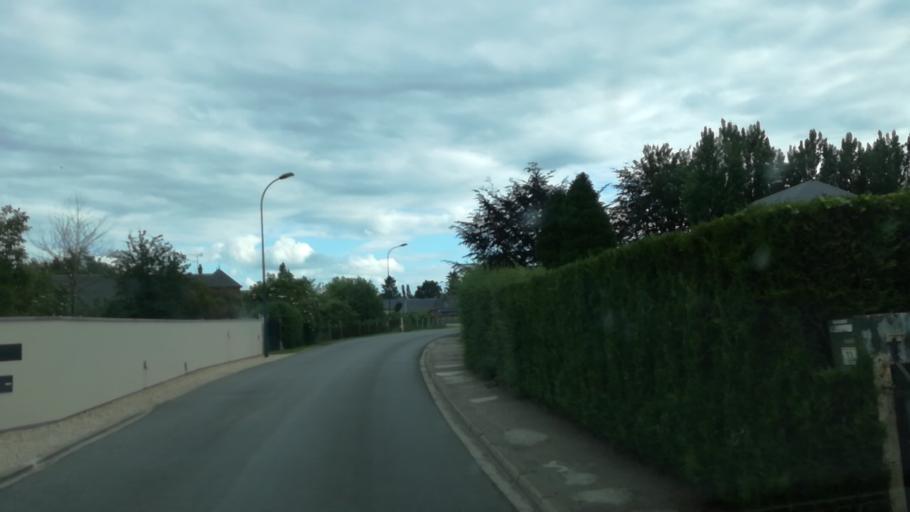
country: FR
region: Haute-Normandie
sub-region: Departement de l'Eure
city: Bourgtheroulde-Infreville
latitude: 49.2257
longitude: 0.8415
